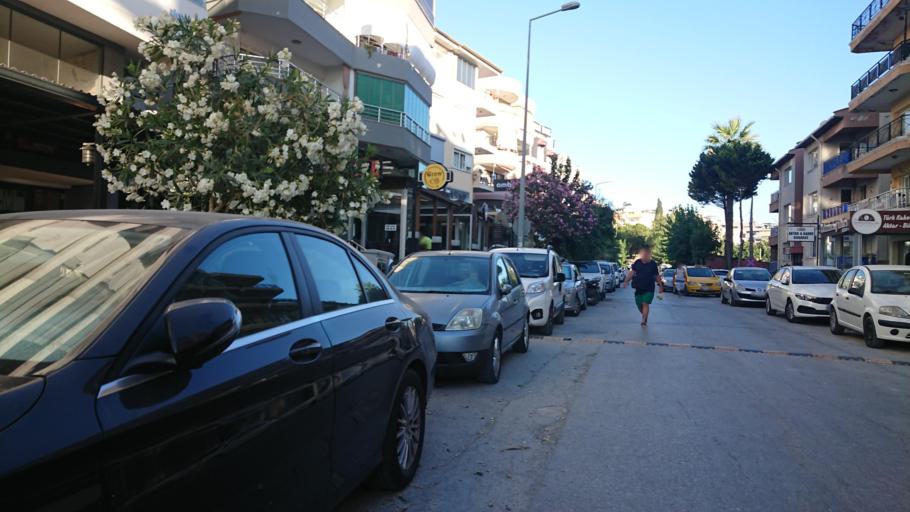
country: TR
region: Aydin
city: Kusadasi
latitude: 37.8650
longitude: 27.2631
